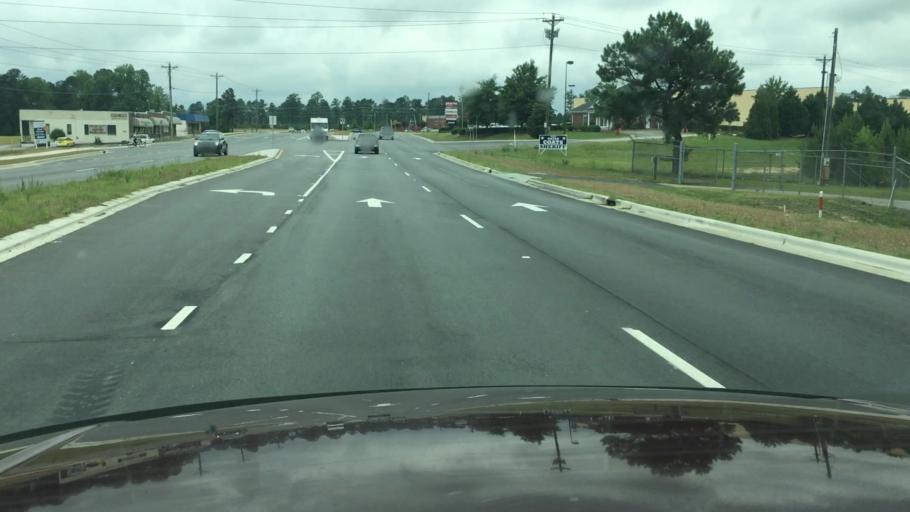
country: US
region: North Carolina
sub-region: Cumberland County
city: Spring Lake
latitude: 35.2526
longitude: -78.9667
